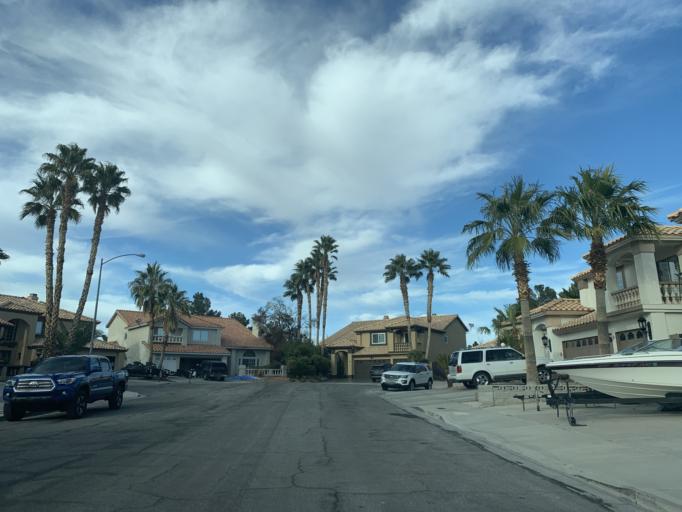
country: US
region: Nevada
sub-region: Clark County
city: Summerlin South
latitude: 36.1289
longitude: -115.3007
